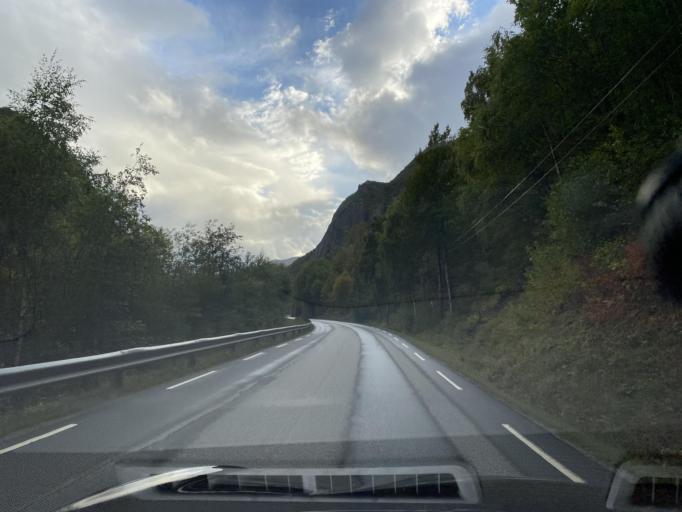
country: NO
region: Oppland
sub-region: Lom
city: Fossbergom
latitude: 61.7847
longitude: 8.4413
